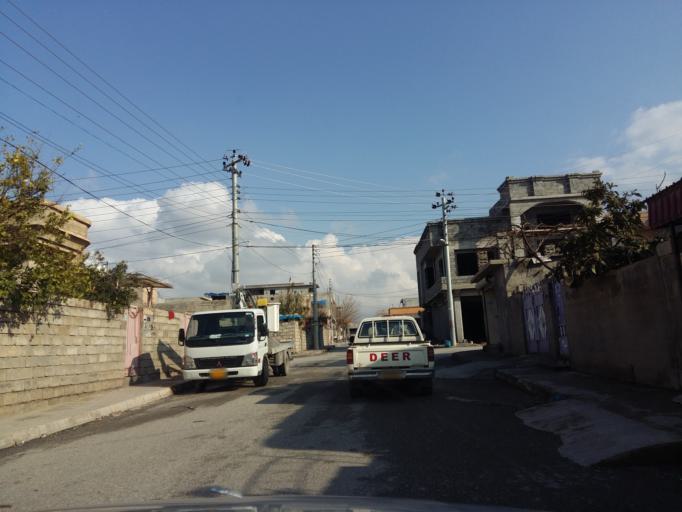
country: IQ
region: As Sulaymaniyah
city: Qeladize
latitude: 36.1771
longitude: 45.1379
